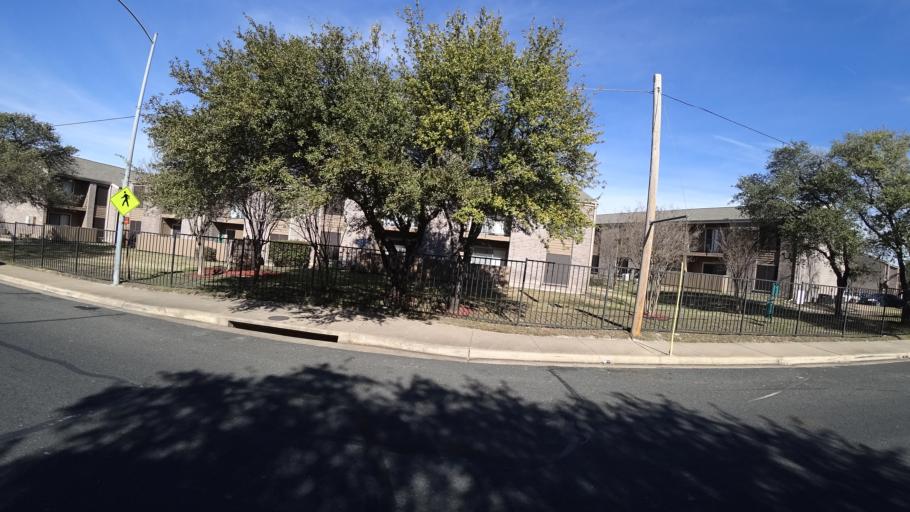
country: US
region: Texas
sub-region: Travis County
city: Wells Branch
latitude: 30.3701
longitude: -97.6901
